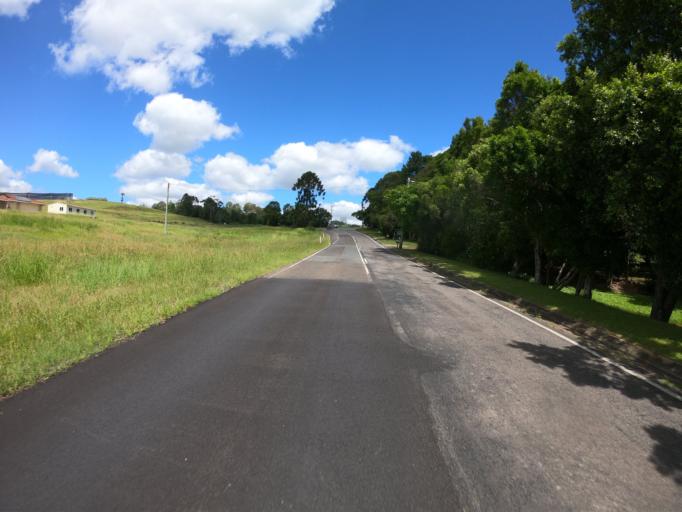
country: AU
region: Queensland
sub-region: Moreton Bay
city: Burpengary
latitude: -27.1502
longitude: 152.9810
